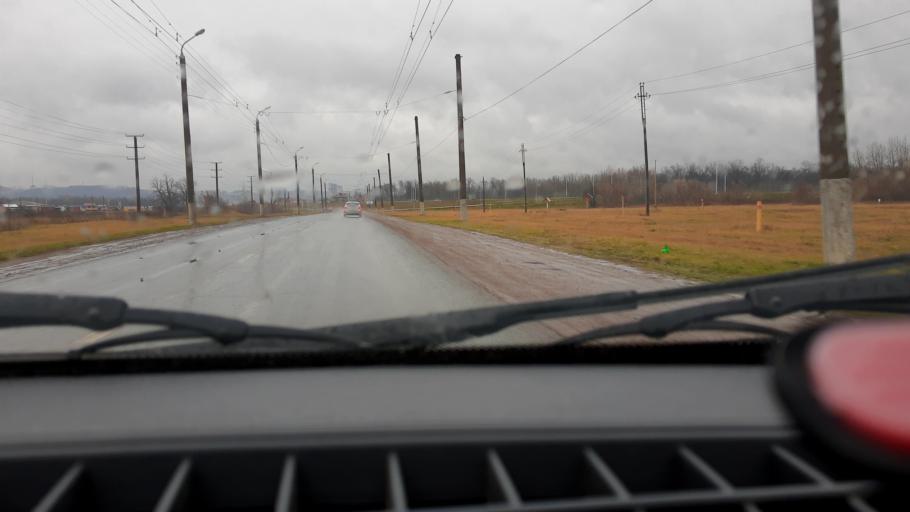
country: RU
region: Bashkortostan
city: Ufa
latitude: 54.7801
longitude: 55.9482
